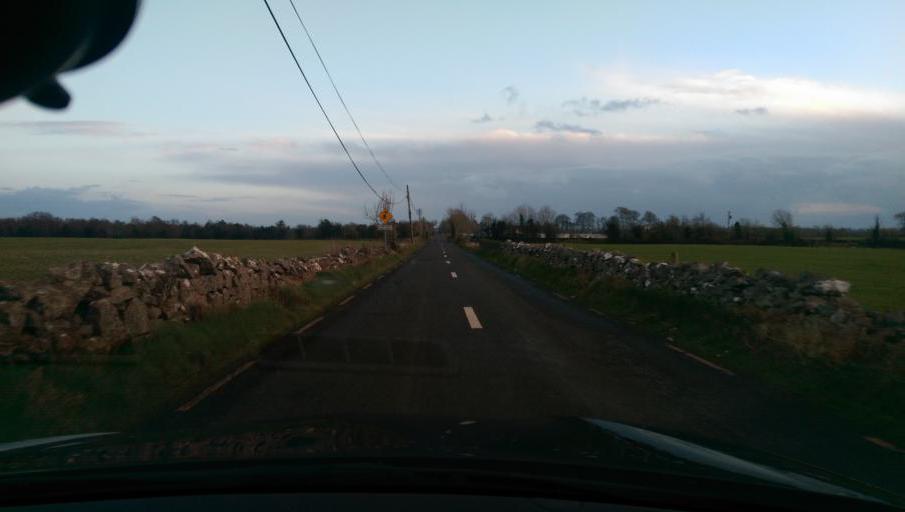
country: IE
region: Connaught
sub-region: County Galway
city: Ballinasloe
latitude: 53.3646
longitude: -8.2598
